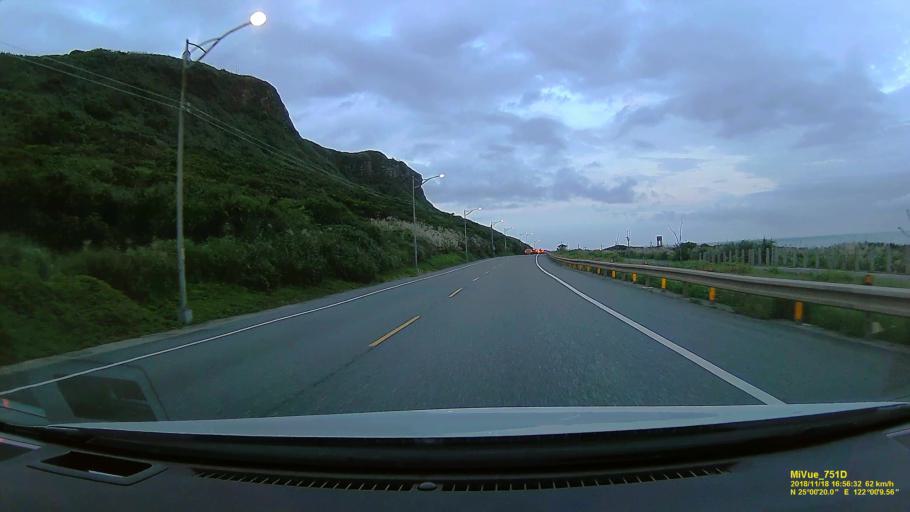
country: TW
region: Taiwan
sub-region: Keelung
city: Keelung
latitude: 25.0058
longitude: 122.0027
